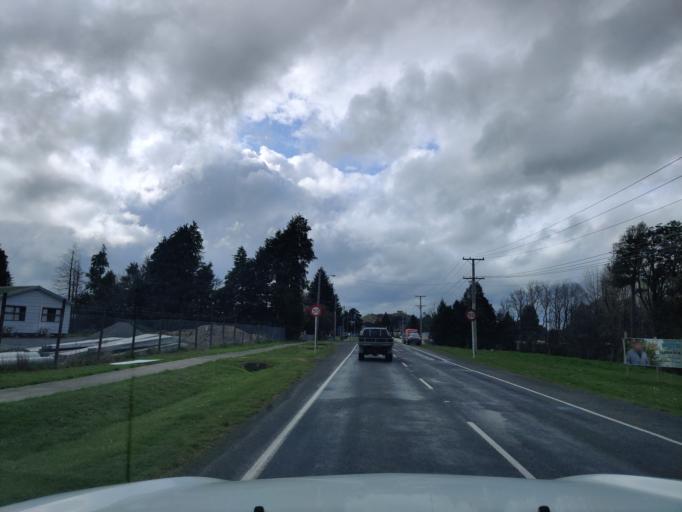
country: NZ
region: Manawatu-Wanganui
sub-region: Ruapehu District
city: Waiouru
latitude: -39.4324
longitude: 175.2827
